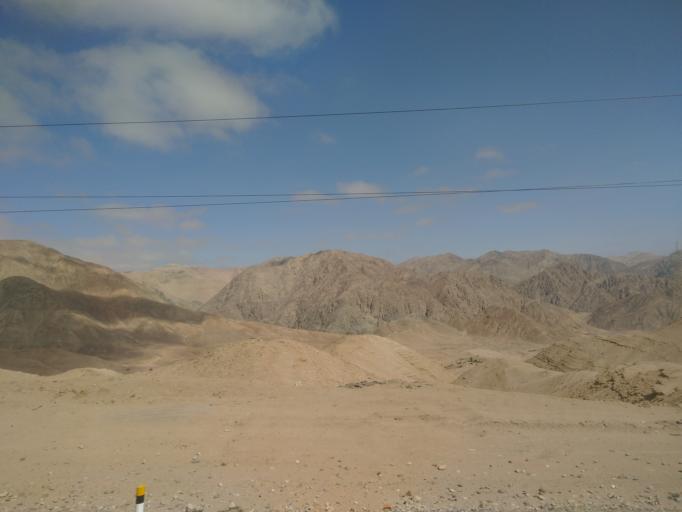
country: PE
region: Moquegua
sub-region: Provincia de Mariscal Nieto
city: Moquegua
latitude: -17.3910
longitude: -71.0147
